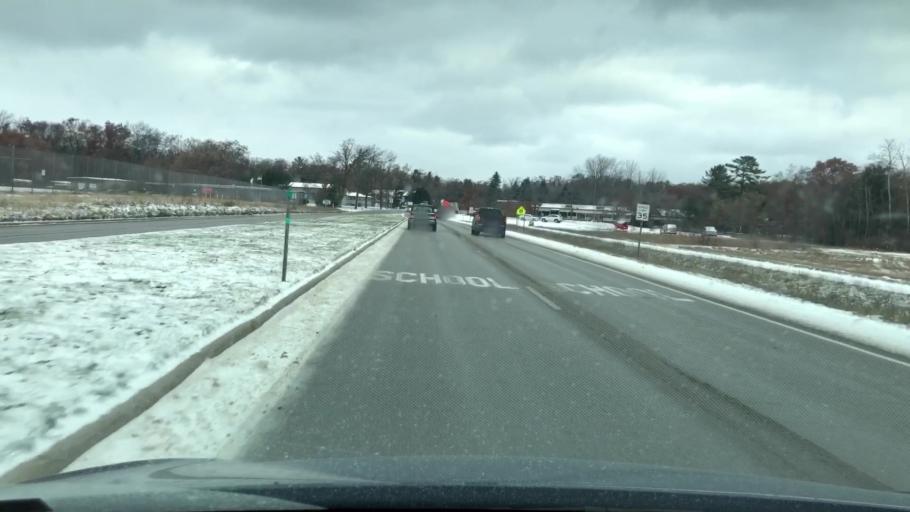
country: US
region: Michigan
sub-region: Grand Traverse County
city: Traverse City
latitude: 44.7405
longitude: -85.5593
